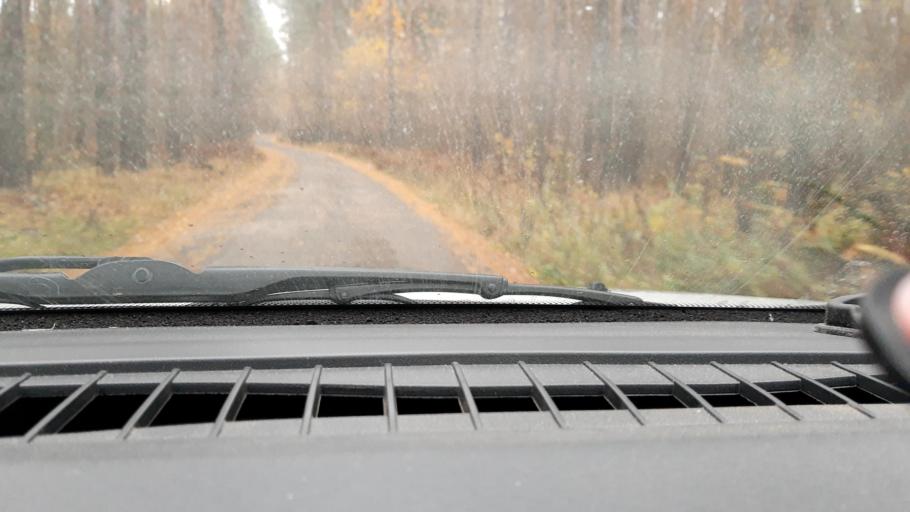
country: RU
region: Nizjnij Novgorod
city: Sitniki
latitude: 56.4183
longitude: 44.0442
